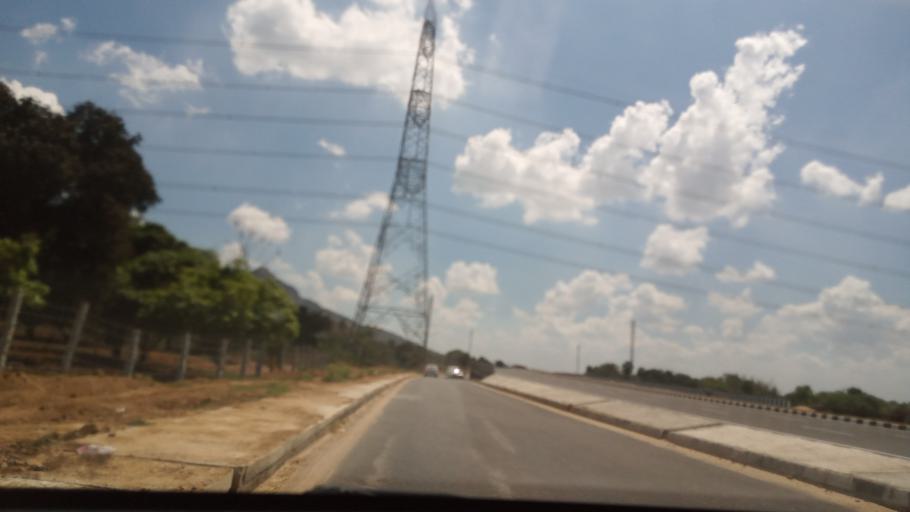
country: IN
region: Andhra Pradesh
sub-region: Chittoor
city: Pakala
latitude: 13.3397
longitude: 79.0808
